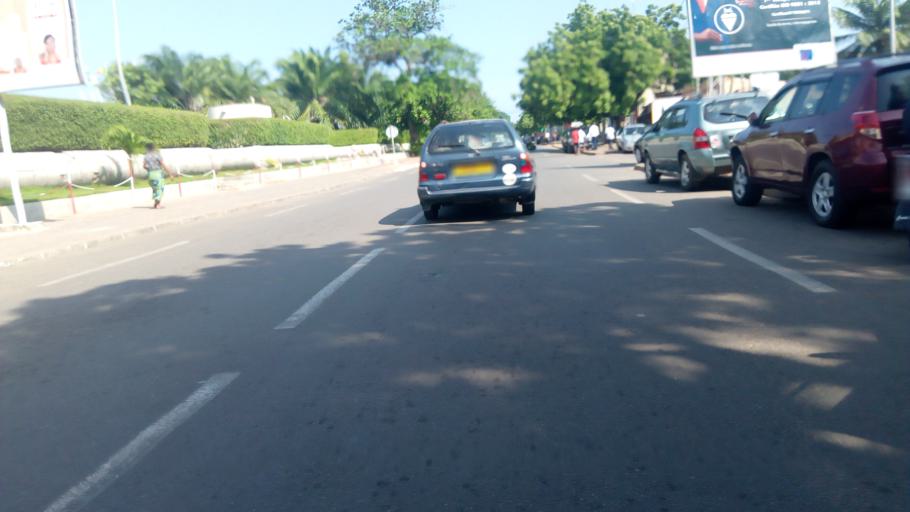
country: TG
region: Maritime
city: Lome
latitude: 6.1362
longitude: 1.2223
